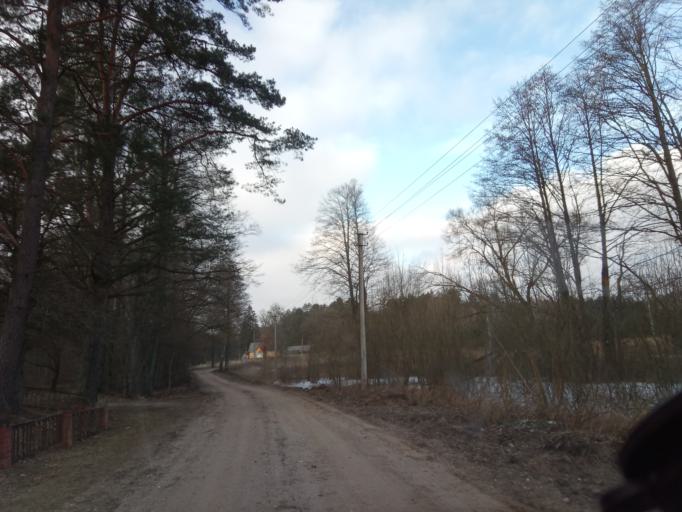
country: LT
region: Alytaus apskritis
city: Druskininkai
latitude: 53.9560
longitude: 24.2912
